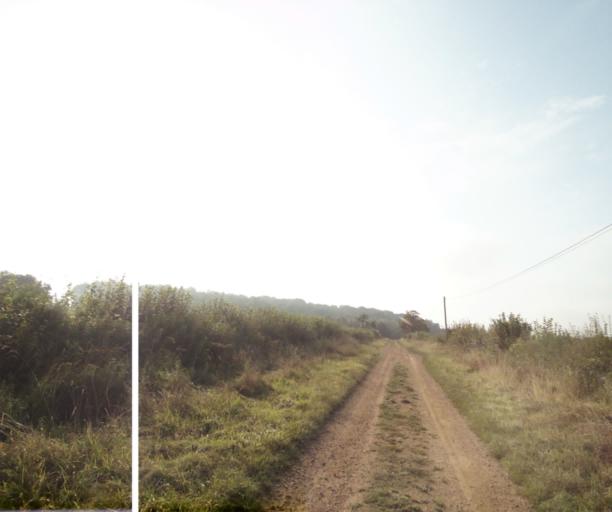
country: FR
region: Bourgogne
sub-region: Departement de Saone-et-Loire
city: Charolles
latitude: 46.4783
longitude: 4.2750
